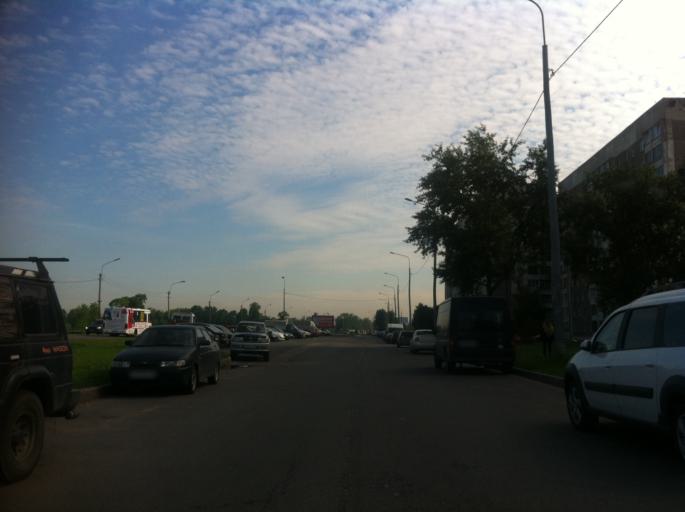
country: RU
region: St.-Petersburg
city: Uritsk
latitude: 59.8293
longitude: 30.1910
